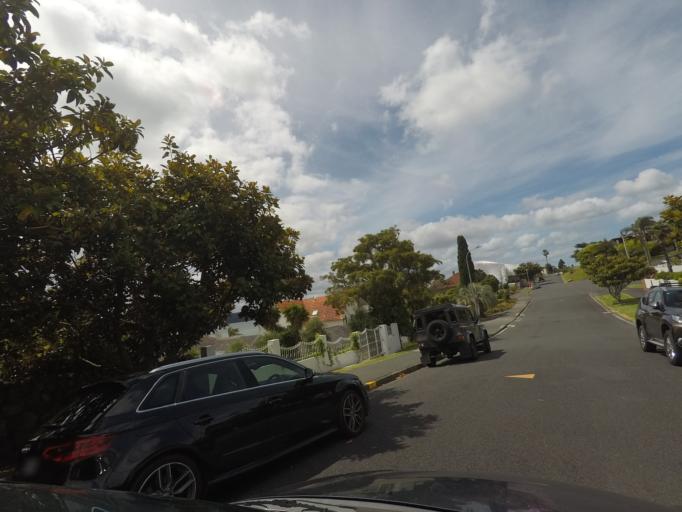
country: NZ
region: Auckland
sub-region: Auckland
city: Auckland
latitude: -36.8464
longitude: 174.7249
